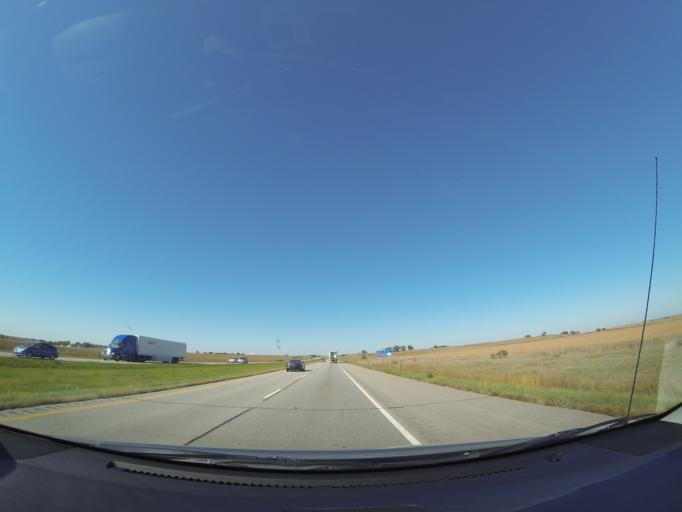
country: US
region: Nebraska
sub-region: Seward County
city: Milford
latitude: 40.8223
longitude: -97.0859
